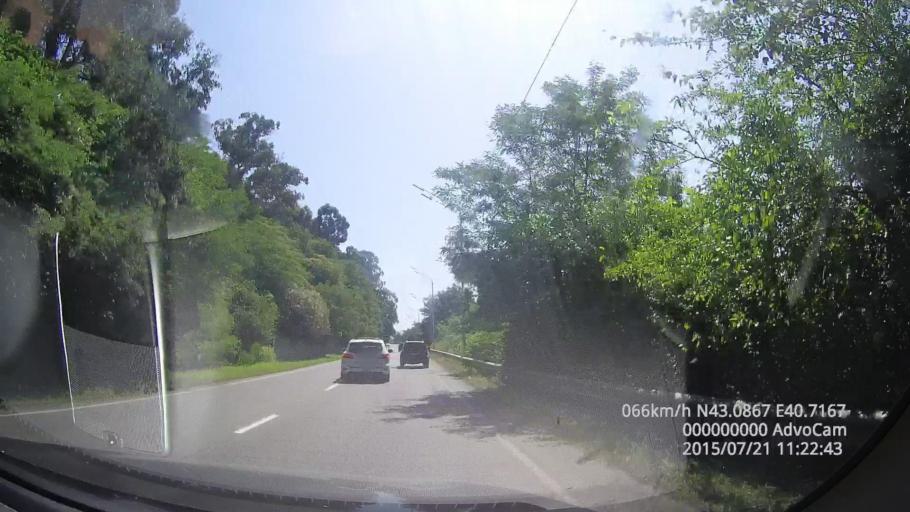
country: GE
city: P'rimorsk'oe
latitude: 43.0866
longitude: 40.7171
